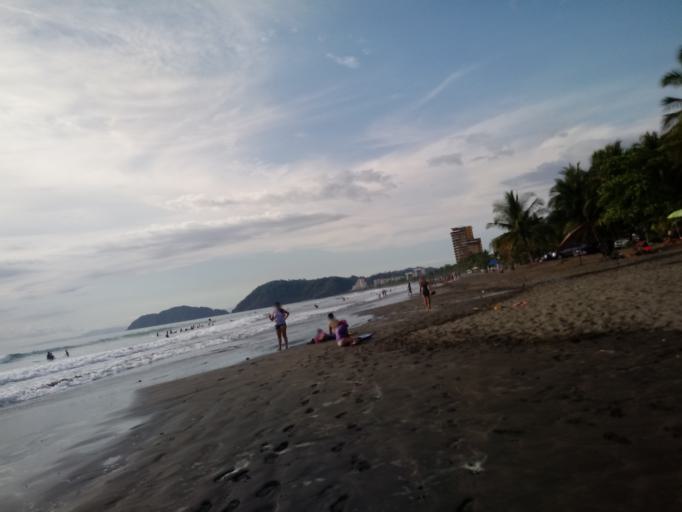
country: CR
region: Puntarenas
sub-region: Canton de Garabito
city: Jaco
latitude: 9.6044
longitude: -84.6227
